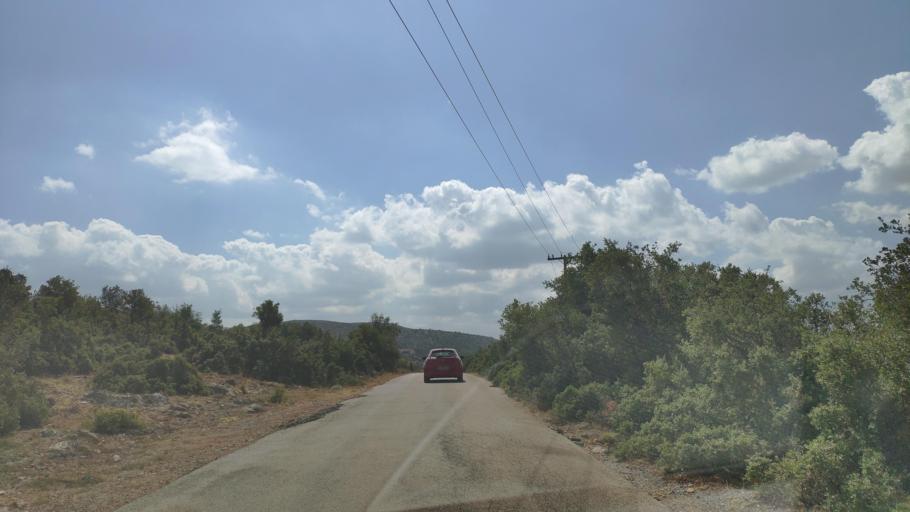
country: GR
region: Peloponnese
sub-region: Nomos Lakonias
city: Kariai
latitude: 37.3030
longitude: 22.4591
